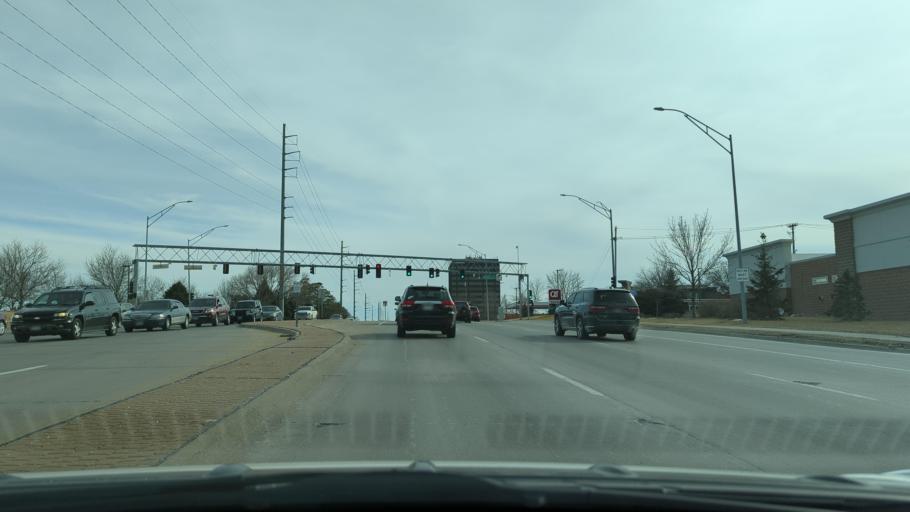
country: US
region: Nebraska
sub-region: Douglas County
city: Ralston
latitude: 41.2441
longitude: -96.0241
